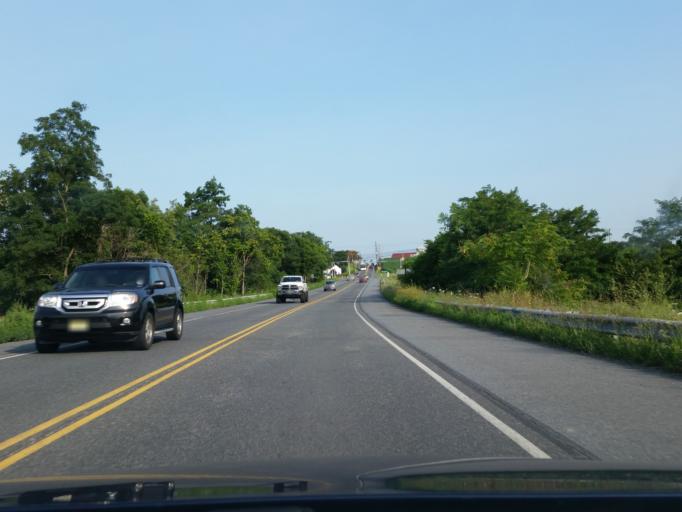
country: US
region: Pennsylvania
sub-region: Dauphin County
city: Skyline View
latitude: 40.3770
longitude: -76.6555
